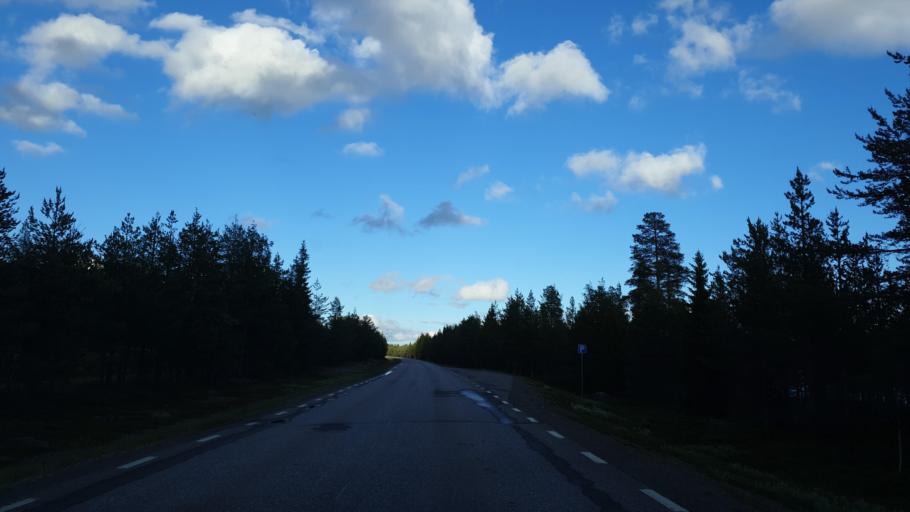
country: SE
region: Norrbotten
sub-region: Arvidsjaurs Kommun
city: Arvidsjaur
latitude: 65.7348
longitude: 18.6316
